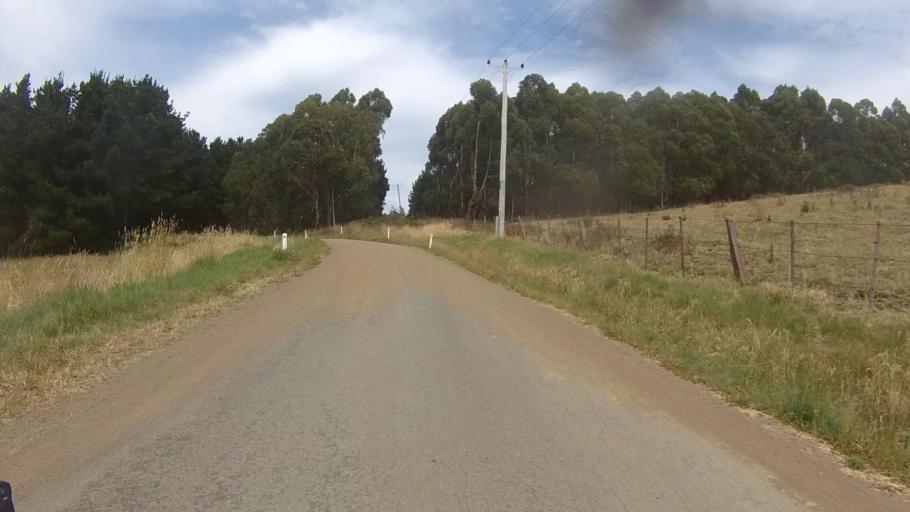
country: AU
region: Tasmania
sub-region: Sorell
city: Sorell
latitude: -42.8103
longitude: 147.8308
